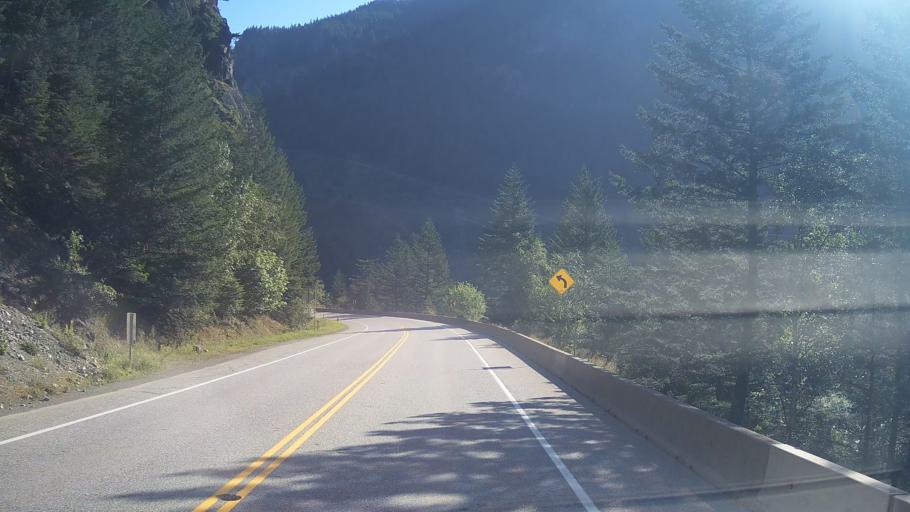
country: CA
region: British Columbia
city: Hope
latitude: 49.5636
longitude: -121.4029
